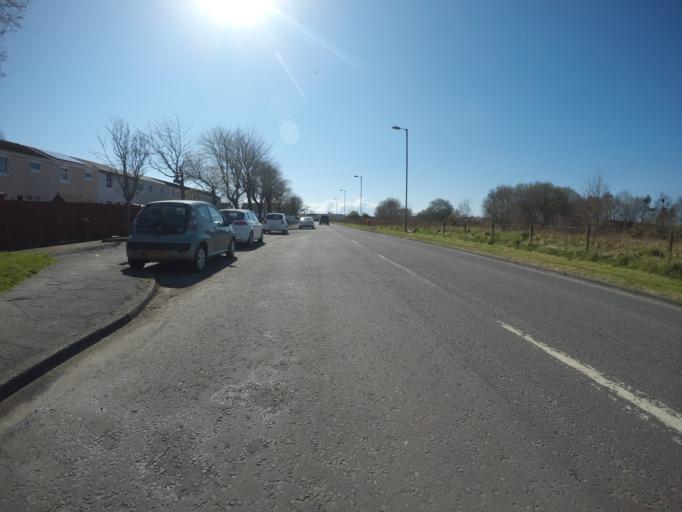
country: GB
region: Scotland
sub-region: North Ayrshire
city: Irvine
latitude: 55.6318
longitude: -4.6677
